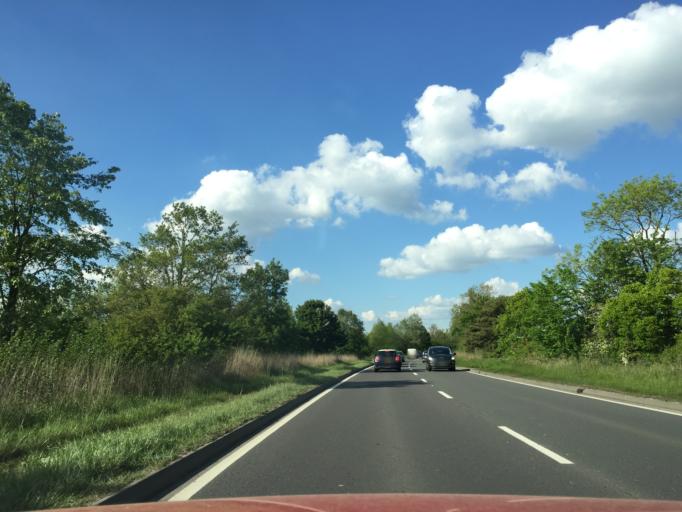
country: GB
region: England
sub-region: Northamptonshire
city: Roade
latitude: 52.1792
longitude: -0.8999
